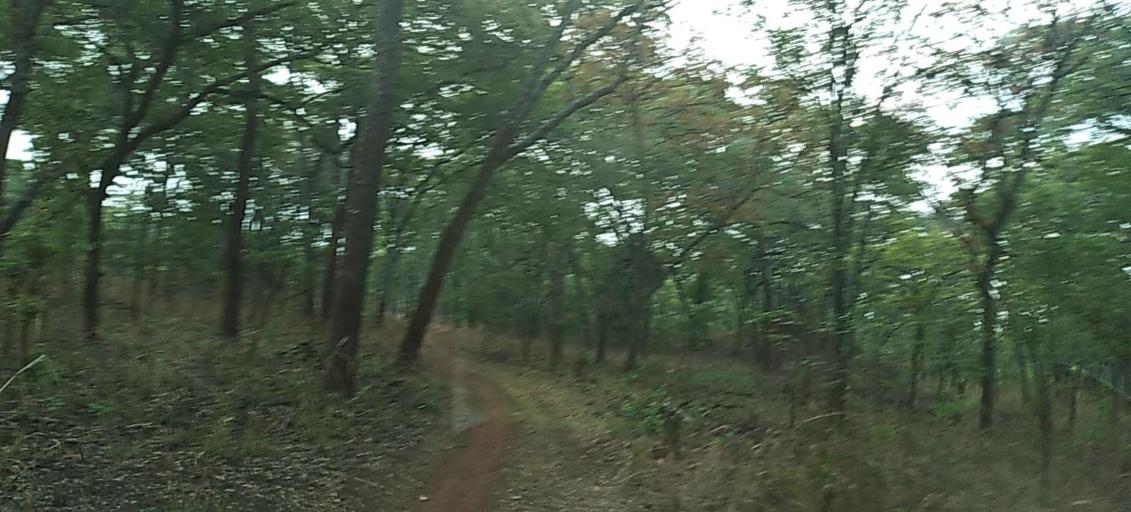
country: ZM
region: North-Western
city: Solwezi
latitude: -12.0452
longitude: 26.0148
